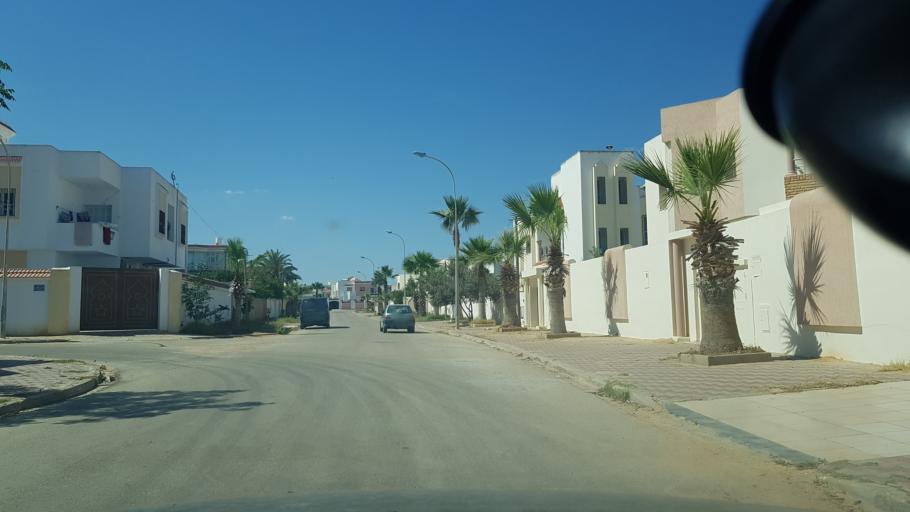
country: TN
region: Safaqis
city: Al Qarmadah
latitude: 34.8292
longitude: 10.7597
